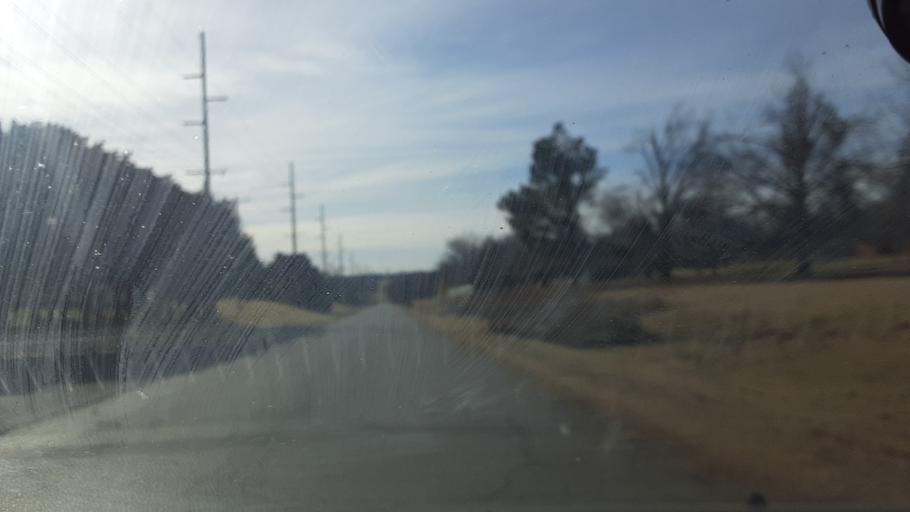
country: US
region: Oklahoma
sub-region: Logan County
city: Guthrie
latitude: 35.8921
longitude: -97.4075
